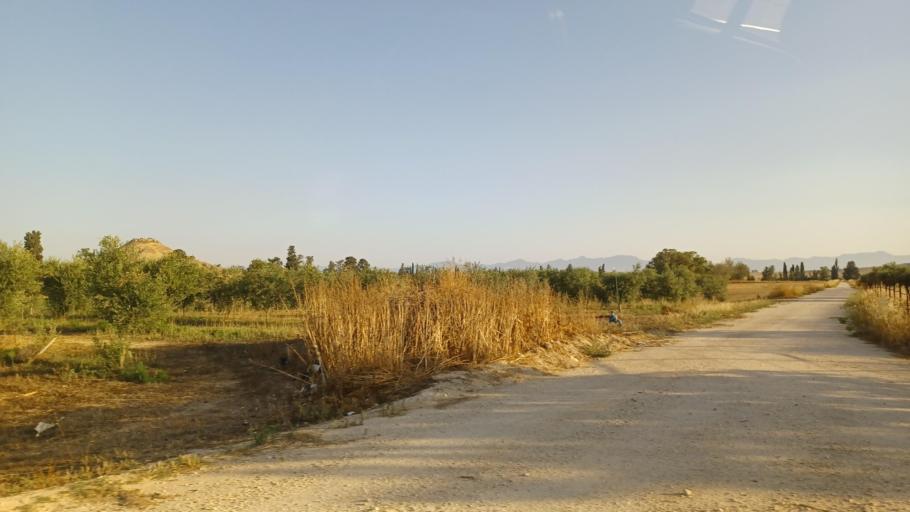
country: CY
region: Larnaka
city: Athienou
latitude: 35.0552
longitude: 33.4988
